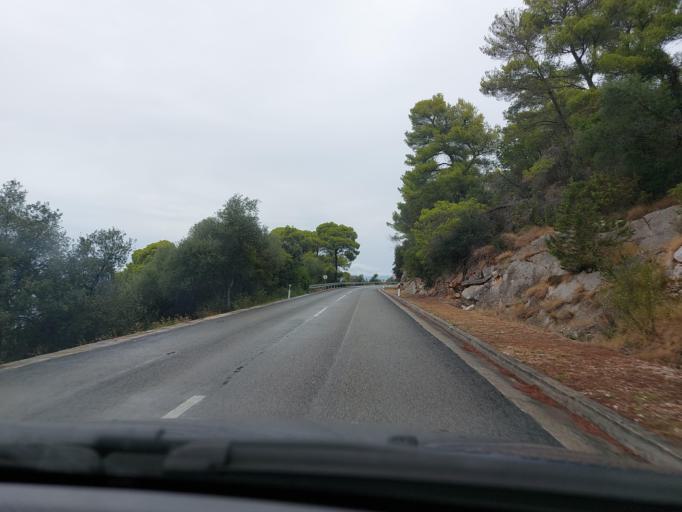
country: HR
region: Dubrovacko-Neretvanska
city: Smokvica
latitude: 42.7680
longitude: 16.8753
